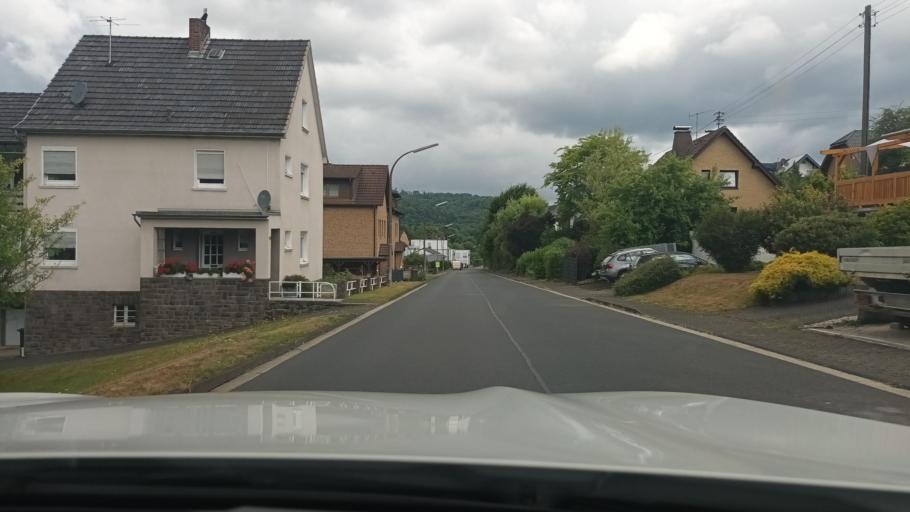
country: DE
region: North Rhine-Westphalia
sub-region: Regierungsbezirk Koln
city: Eitorf
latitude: 50.7713
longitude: 7.4311
